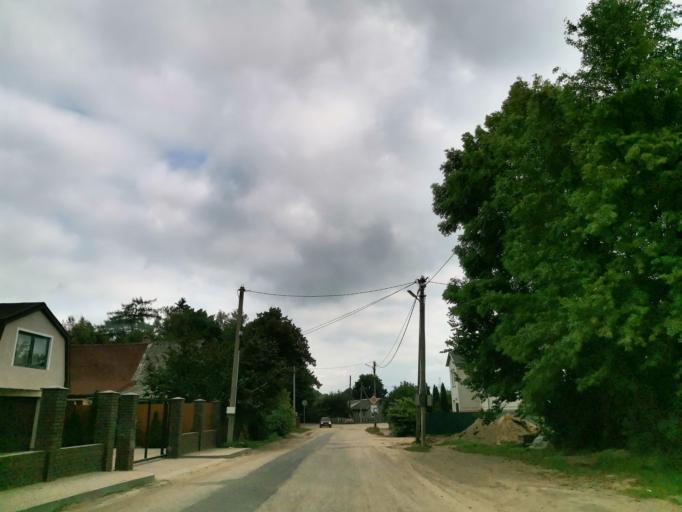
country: RU
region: Kaliningrad
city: Chernyakhovsk
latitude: 54.6620
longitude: 21.8438
